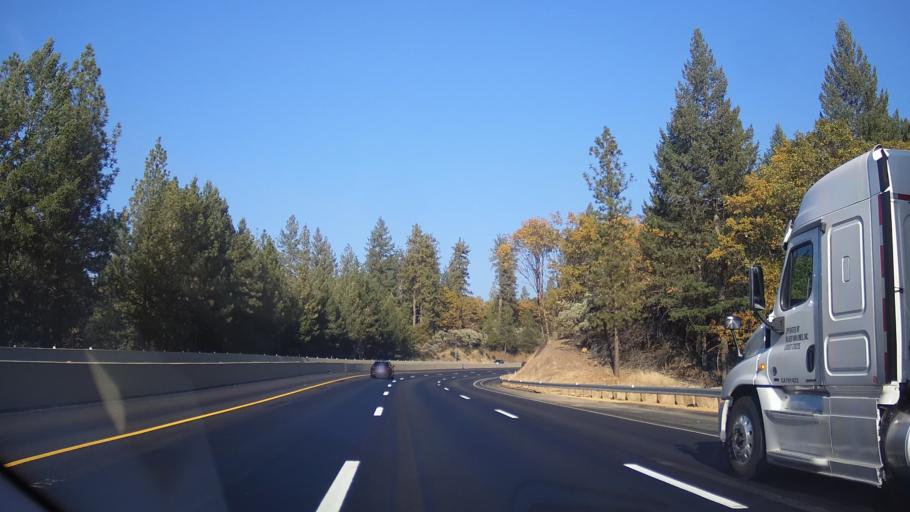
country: US
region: California
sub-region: Placer County
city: Colfax
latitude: 39.1372
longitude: -120.9294
